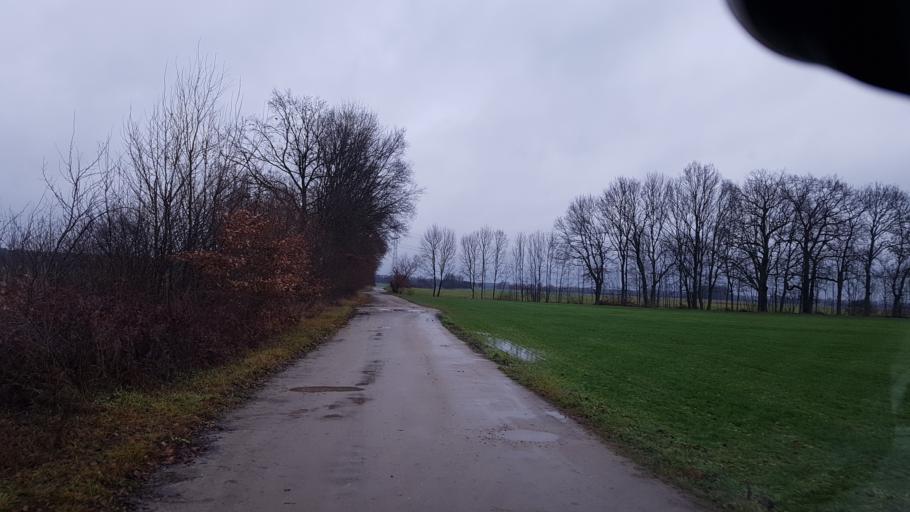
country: DE
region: Brandenburg
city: Sallgast
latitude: 51.6223
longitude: 13.8455
